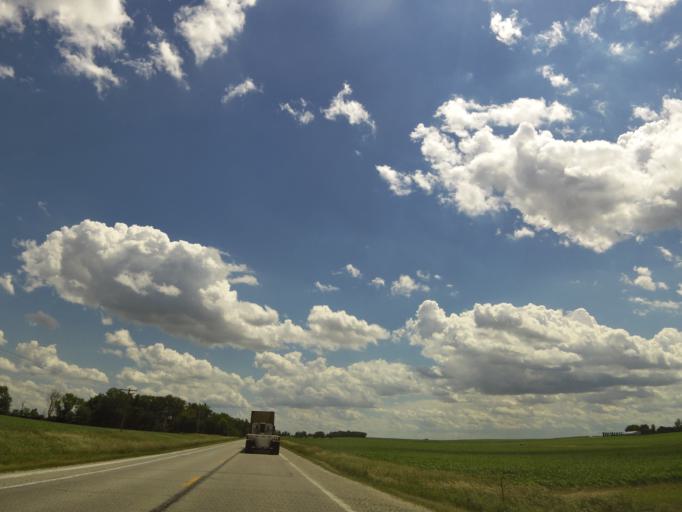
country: US
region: Iowa
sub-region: Buchanan County
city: Independence
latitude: 42.3553
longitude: -91.8892
